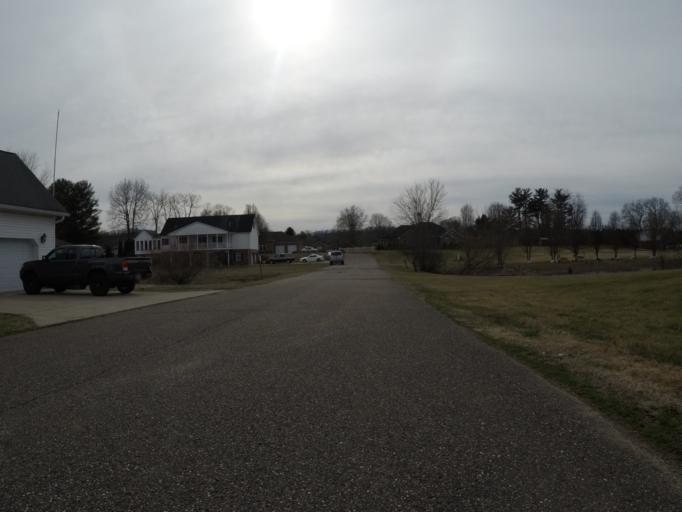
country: US
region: West Virginia
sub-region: Cabell County
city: Pea Ridge
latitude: 38.4507
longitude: -82.3407
